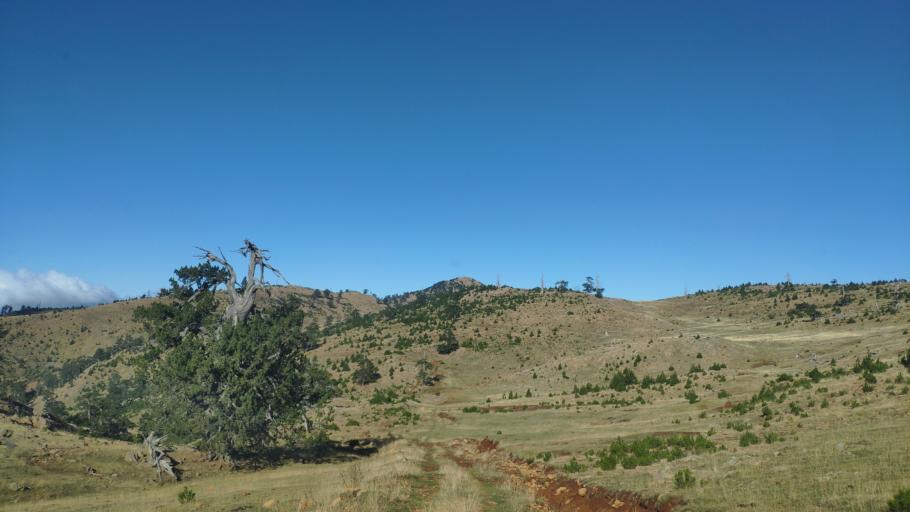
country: GR
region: Epirus
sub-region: Nomos Ioanninon
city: Metsovo
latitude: 39.8615
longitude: 21.1511
